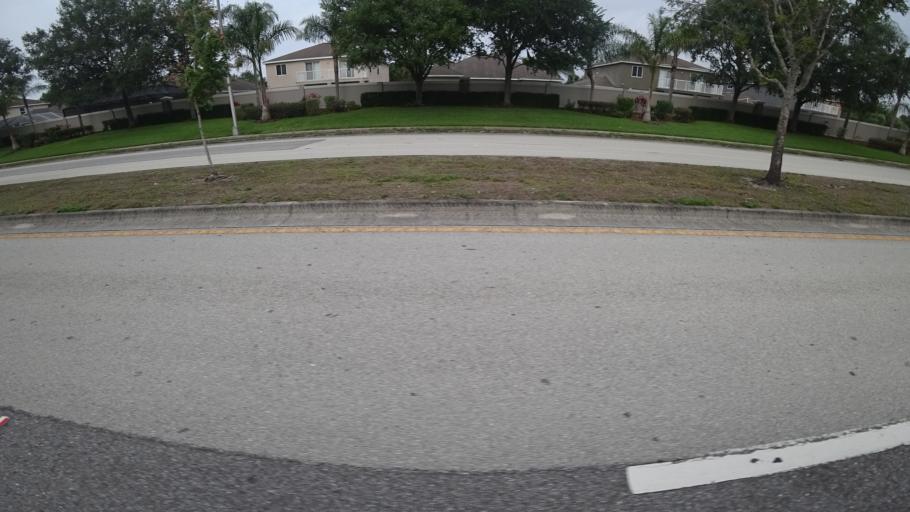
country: US
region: Florida
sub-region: Manatee County
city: Samoset
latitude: 27.4375
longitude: -82.5054
